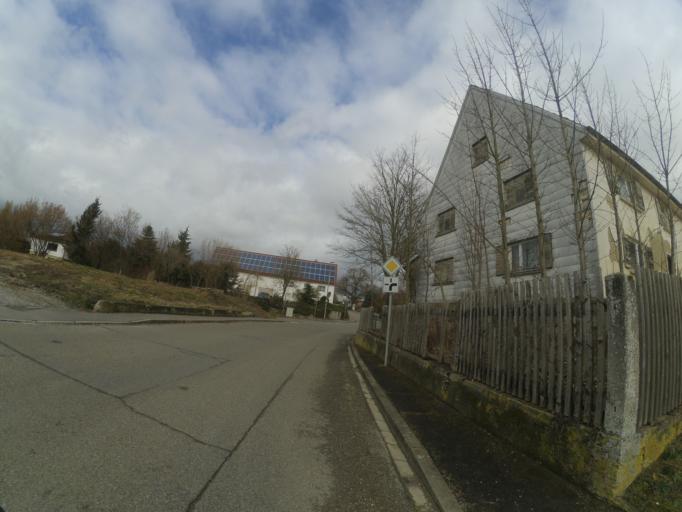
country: DE
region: Bavaria
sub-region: Swabia
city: Vohringen
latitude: 48.2956
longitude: 10.1042
